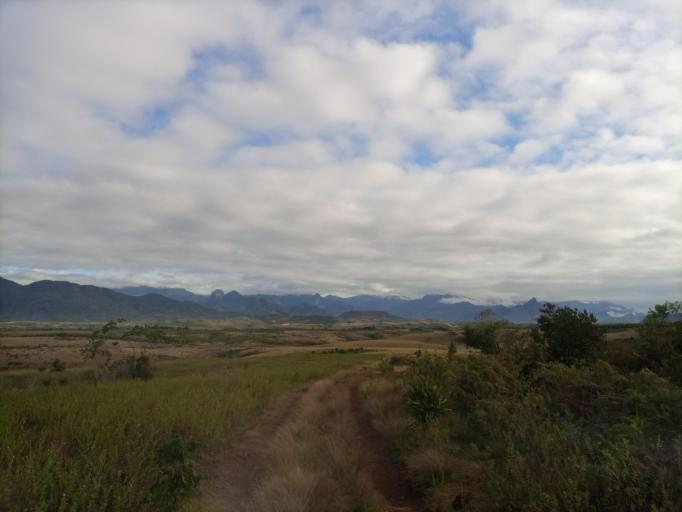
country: MG
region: Anosy
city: Fort Dauphin
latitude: -24.3093
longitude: 47.2484
